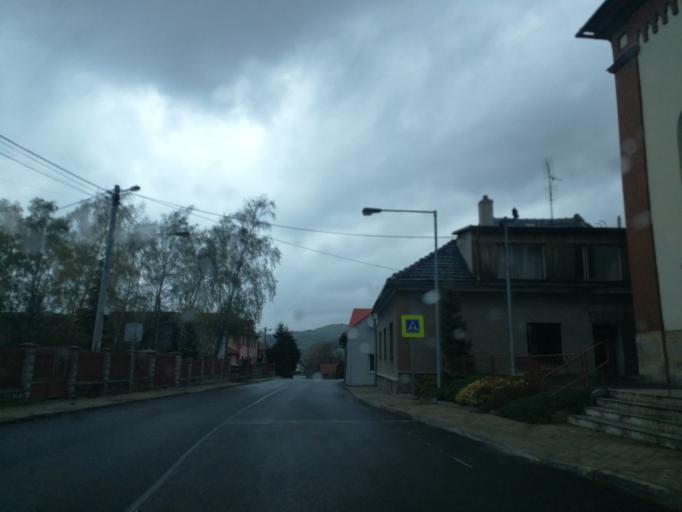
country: CZ
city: Morkov
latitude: 49.5380
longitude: 18.0595
